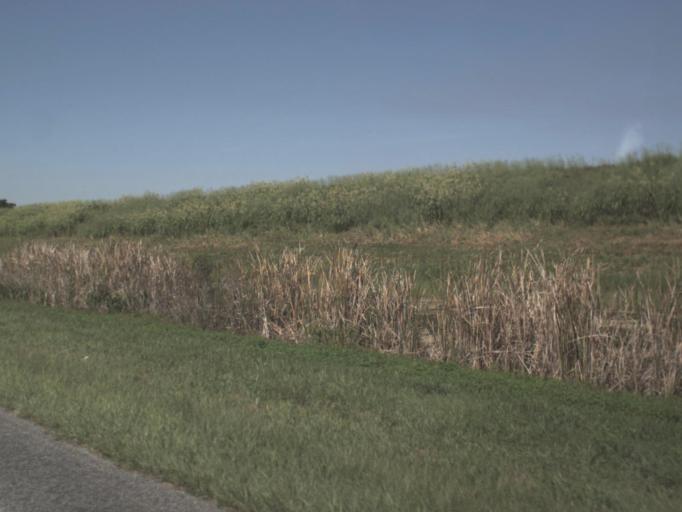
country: US
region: Florida
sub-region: Hendry County
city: Clewiston
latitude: 26.7479
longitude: -80.8955
